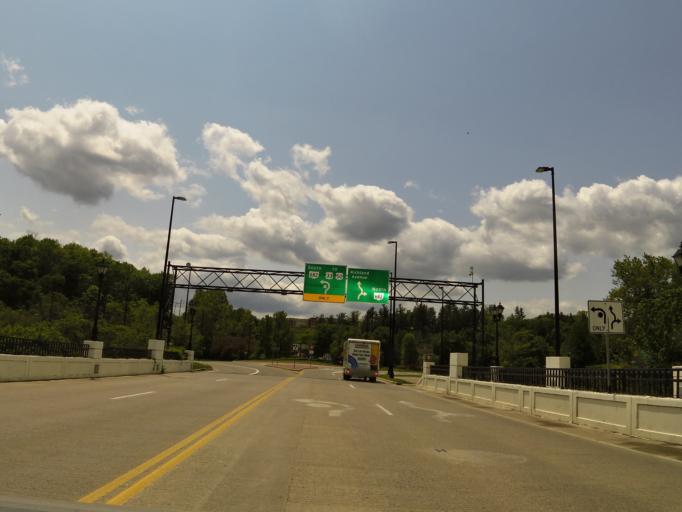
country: US
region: Ohio
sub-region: Athens County
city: Athens
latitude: 39.3200
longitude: -82.1053
